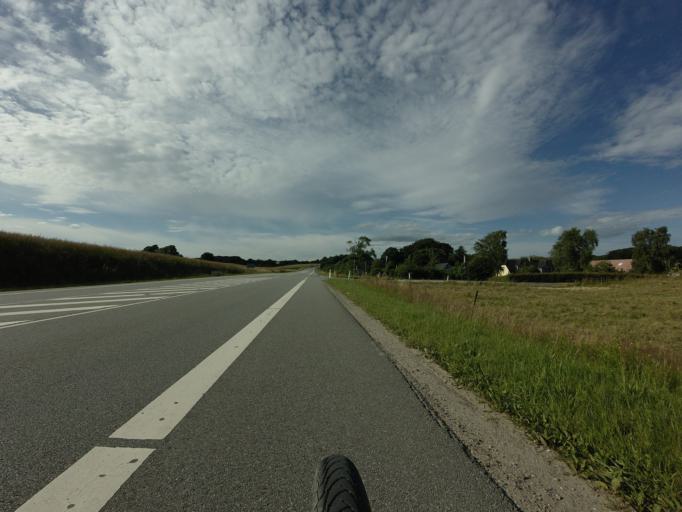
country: DK
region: Central Jutland
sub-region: Skanderborg Kommune
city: Stilling
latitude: 56.0890
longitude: 9.9704
